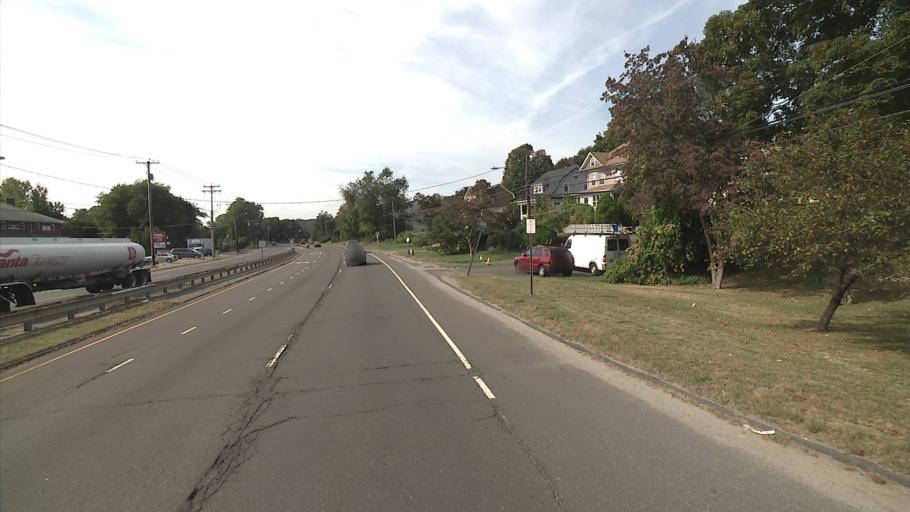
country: US
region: Connecticut
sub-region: New Haven County
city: Derby
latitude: 41.3102
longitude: -73.0623
